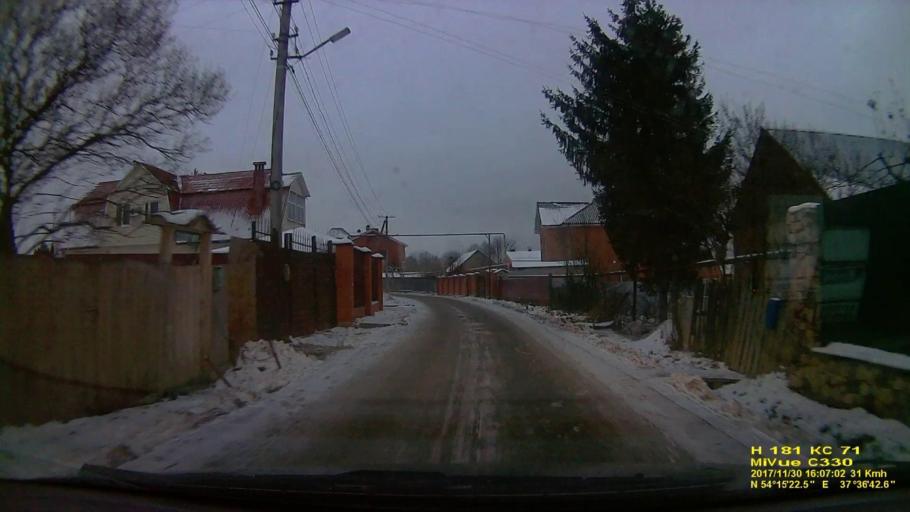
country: RU
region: Tula
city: Gorelki
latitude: 54.2563
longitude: 37.6116
